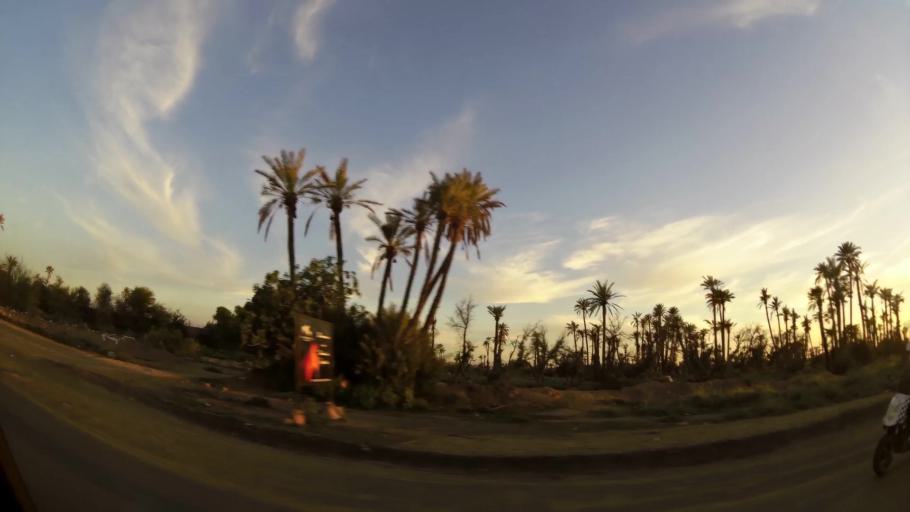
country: MA
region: Marrakech-Tensift-Al Haouz
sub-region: Marrakech
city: Marrakesh
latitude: 31.6880
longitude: -7.9986
